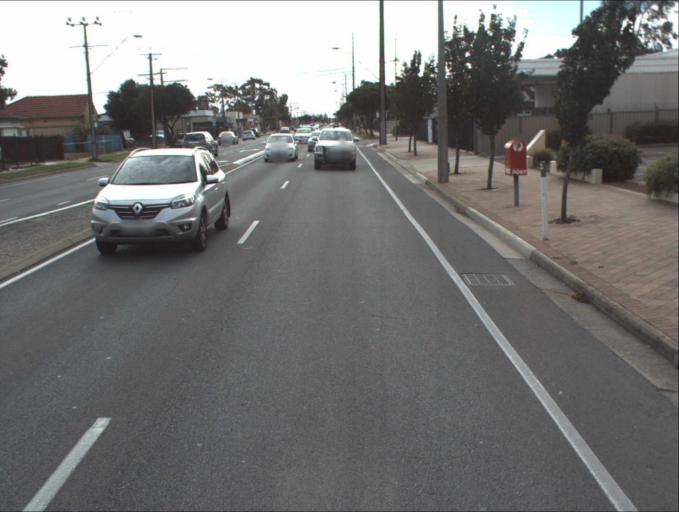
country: AU
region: South Australia
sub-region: Charles Sturt
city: Royal Park
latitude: -34.8767
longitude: 138.5127
